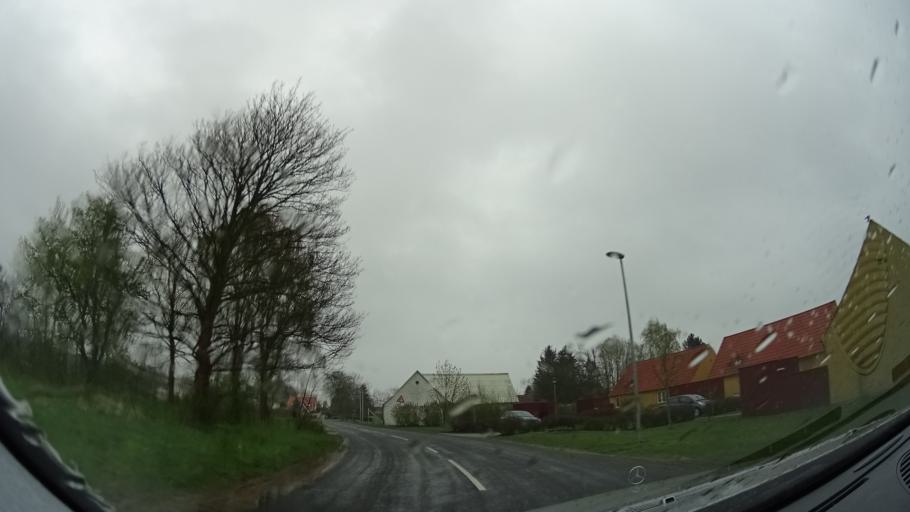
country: DK
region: Zealand
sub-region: Holbaek Kommune
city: Vipperod
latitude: 55.7046
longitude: 11.7749
